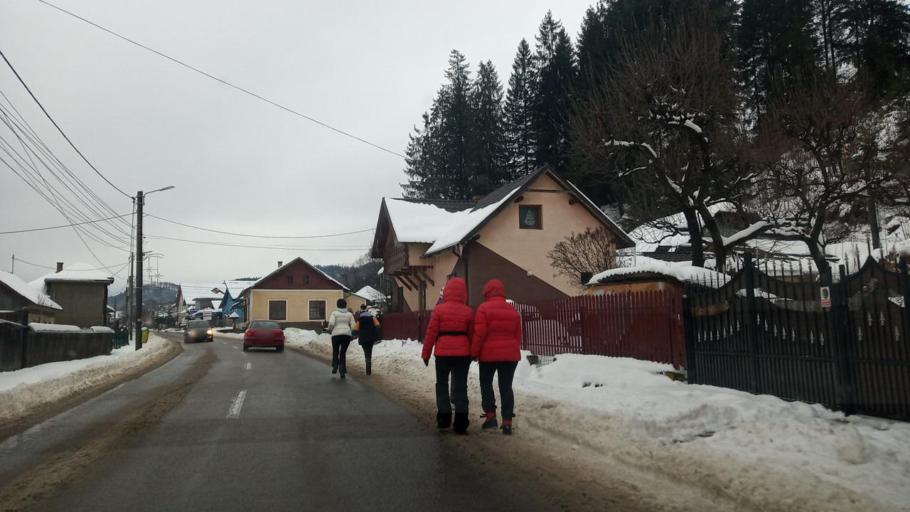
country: RO
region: Suceava
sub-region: Oras Gura Humorului
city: Gura Humorului
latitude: 47.5284
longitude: 25.8637
